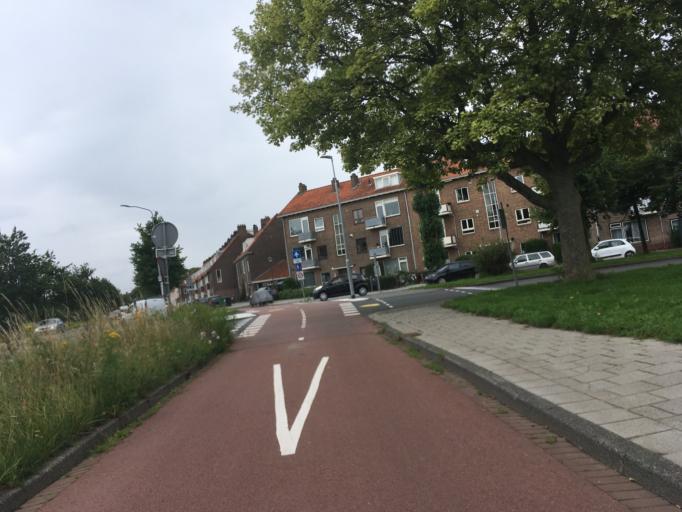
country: NL
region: North Holland
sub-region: Gemeente Bloemendaal
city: Bloemendaal
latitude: 52.4142
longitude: 4.6568
